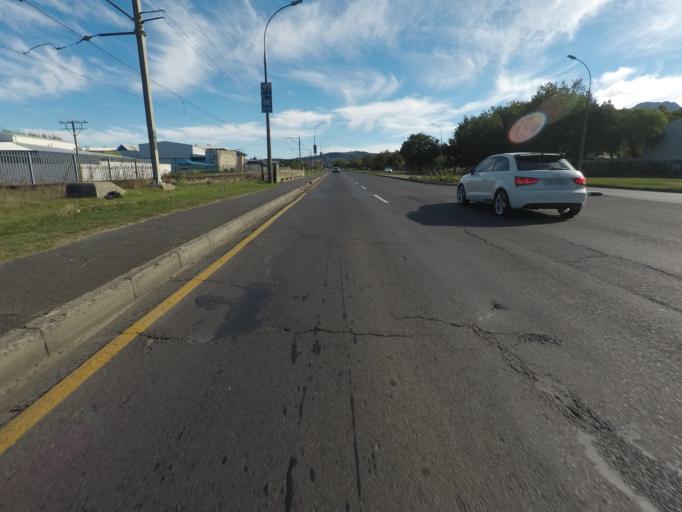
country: ZA
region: Western Cape
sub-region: Cape Winelands District Municipality
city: Stellenbosch
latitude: -33.9301
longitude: 18.8535
